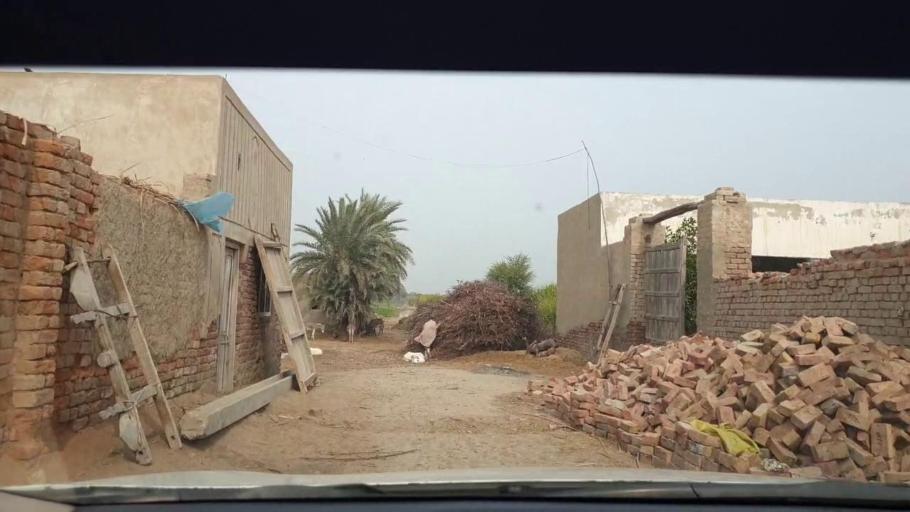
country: PK
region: Sindh
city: Berani
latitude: 25.8342
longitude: 68.8312
